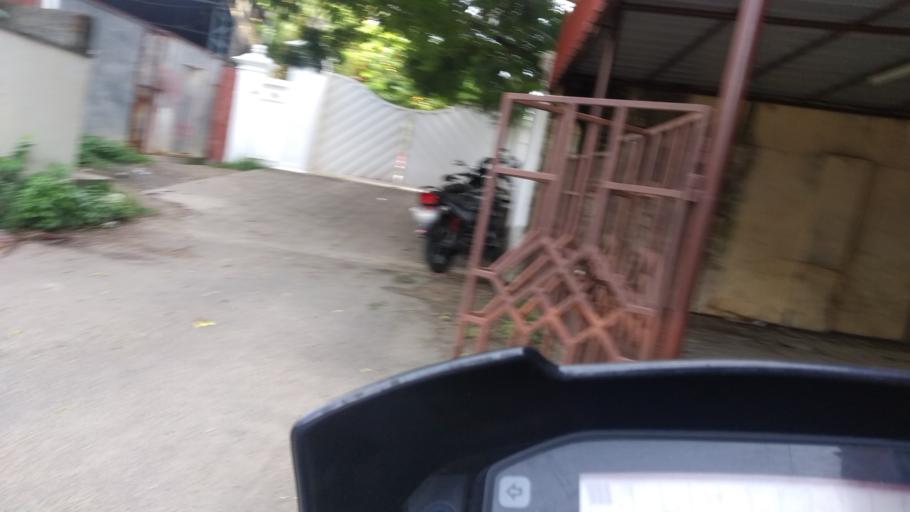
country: IN
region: Kerala
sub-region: Ernakulam
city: Elur
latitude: 10.0063
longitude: 76.2977
